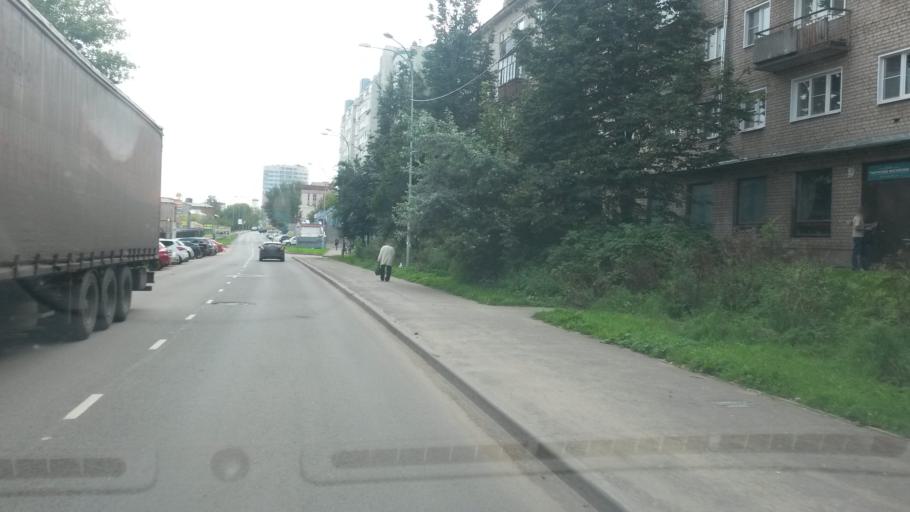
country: RU
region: Ivanovo
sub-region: Gorod Ivanovo
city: Ivanovo
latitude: 57.0034
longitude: 40.9649
